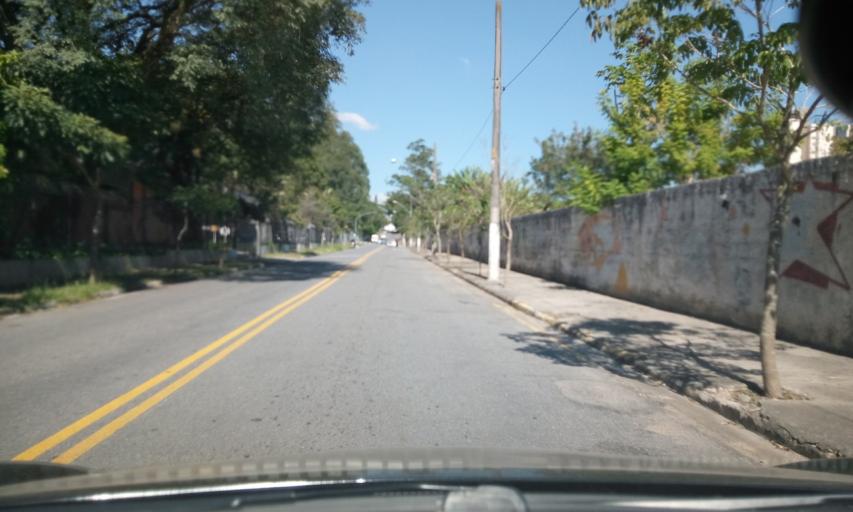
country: BR
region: Sao Paulo
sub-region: Sao Bernardo Do Campo
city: Sao Bernardo do Campo
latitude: -23.7129
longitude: -46.5776
